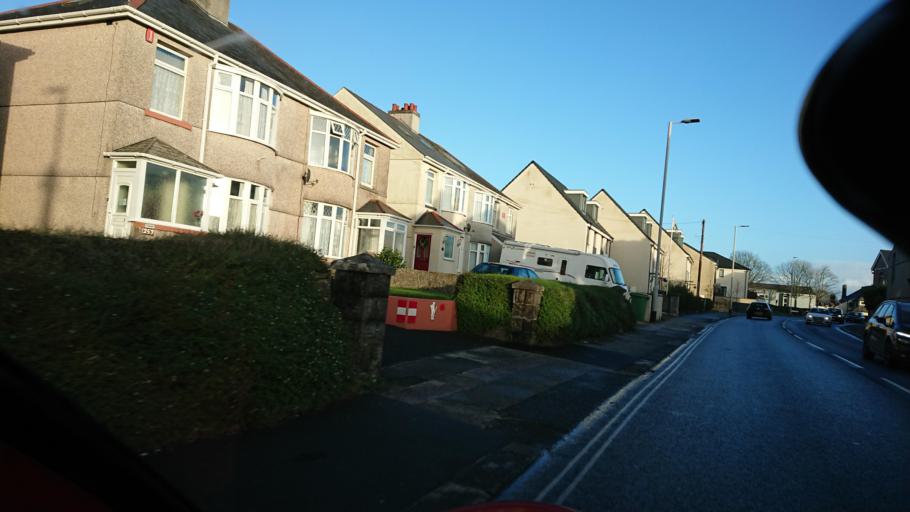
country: GB
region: England
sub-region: Plymouth
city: Plymouth
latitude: 50.3973
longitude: -4.1485
